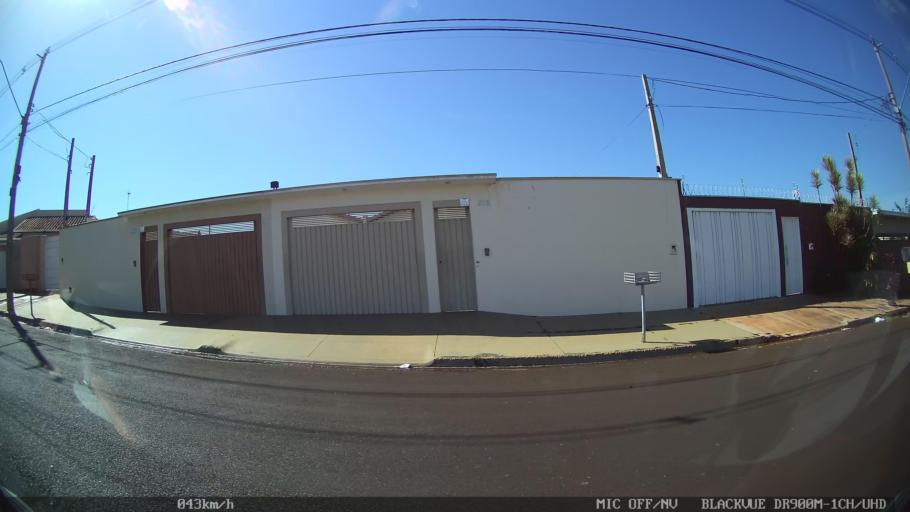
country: BR
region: Sao Paulo
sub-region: Batatais
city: Batatais
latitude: -20.8874
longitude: -47.5656
